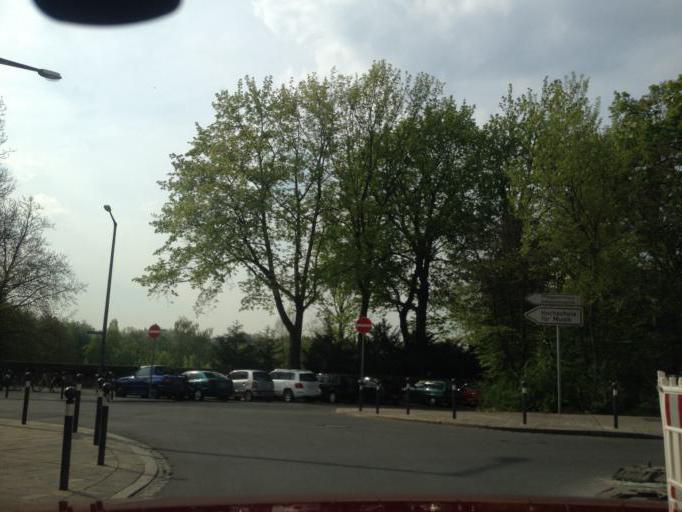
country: DE
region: Bavaria
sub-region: Regierungsbezirk Mittelfranken
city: Nuernberg
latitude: 49.4586
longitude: 11.1055
